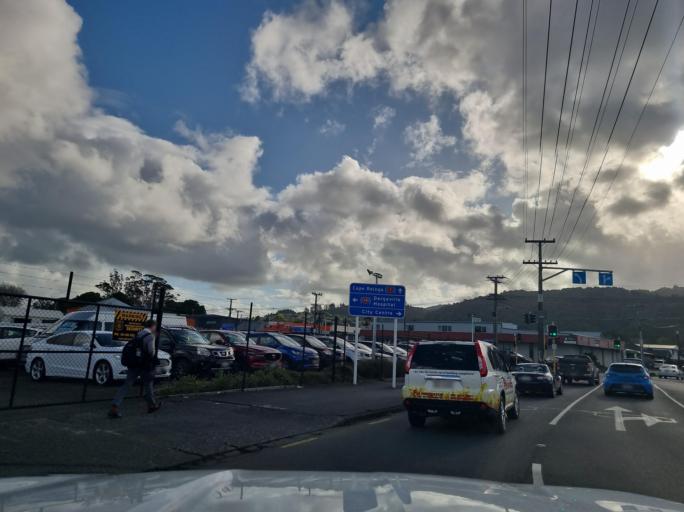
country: NZ
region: Northland
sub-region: Whangarei
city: Whangarei
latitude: -35.7277
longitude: 174.3172
